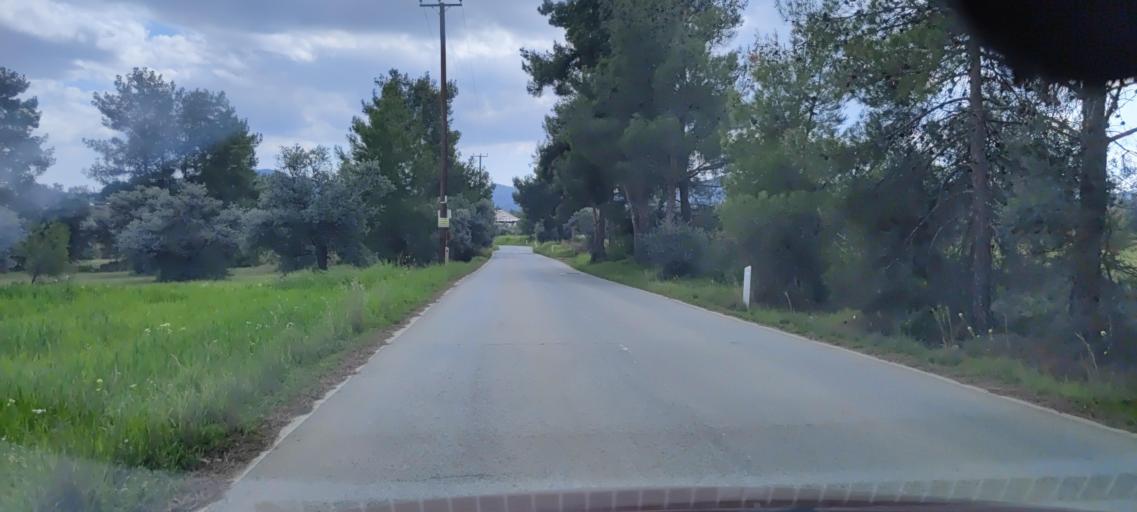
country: CY
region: Lefkosia
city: Lythrodontas
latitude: 34.9653
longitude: 33.2926
